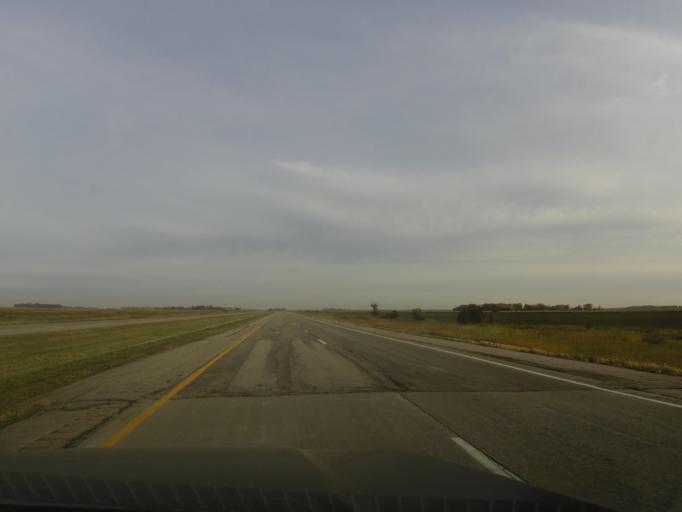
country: US
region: Minnesota
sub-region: Kittson County
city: Hallock
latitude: 48.7332
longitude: -97.1956
